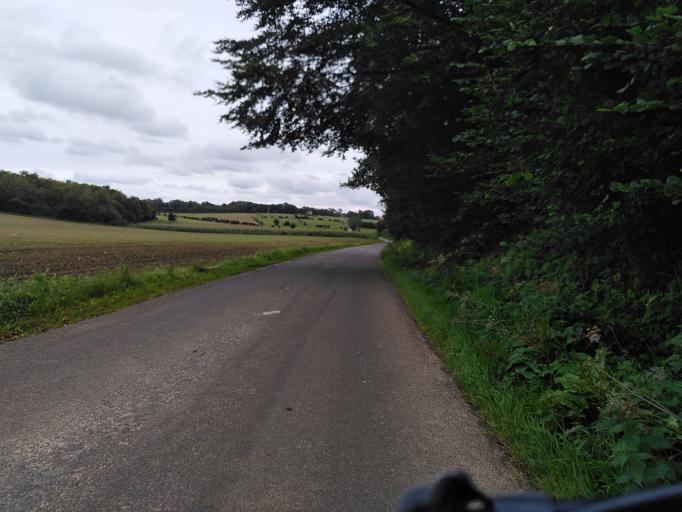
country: FR
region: Nord-Pas-de-Calais
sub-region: Departement du Pas-de-Calais
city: Desvres
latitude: 50.6628
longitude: 1.8817
